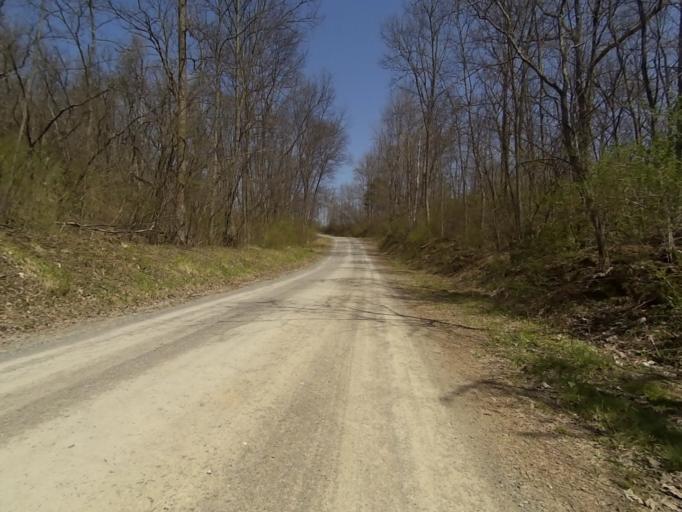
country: US
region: Pennsylvania
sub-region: Blair County
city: Williamsburg
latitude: 40.5449
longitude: -78.1550
